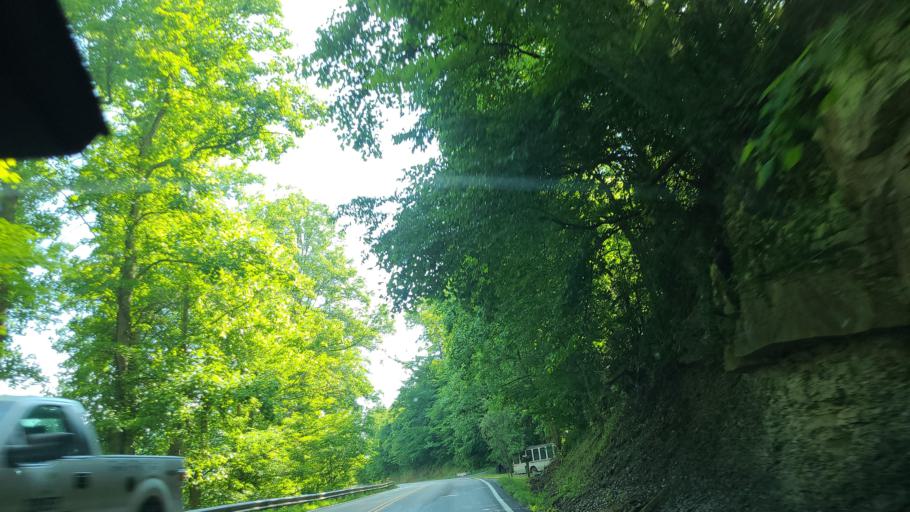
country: US
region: Kentucky
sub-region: Bell County
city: Pineville
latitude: 36.7200
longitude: -83.8103
